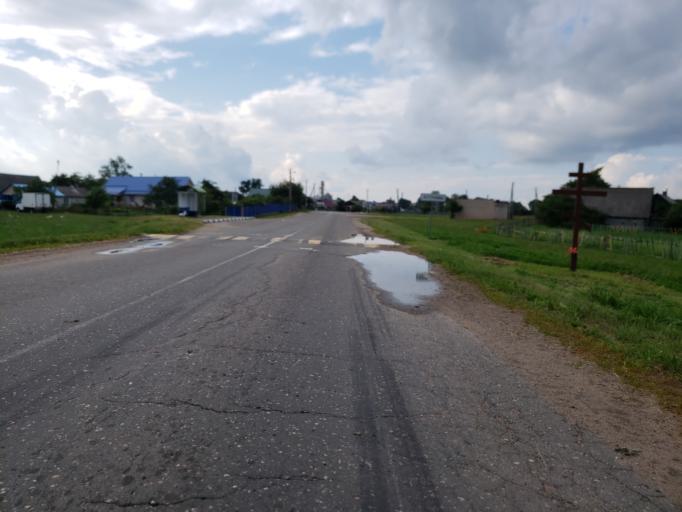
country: BY
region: Minsk
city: Chervyen'
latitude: 53.7288
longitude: 28.3893
